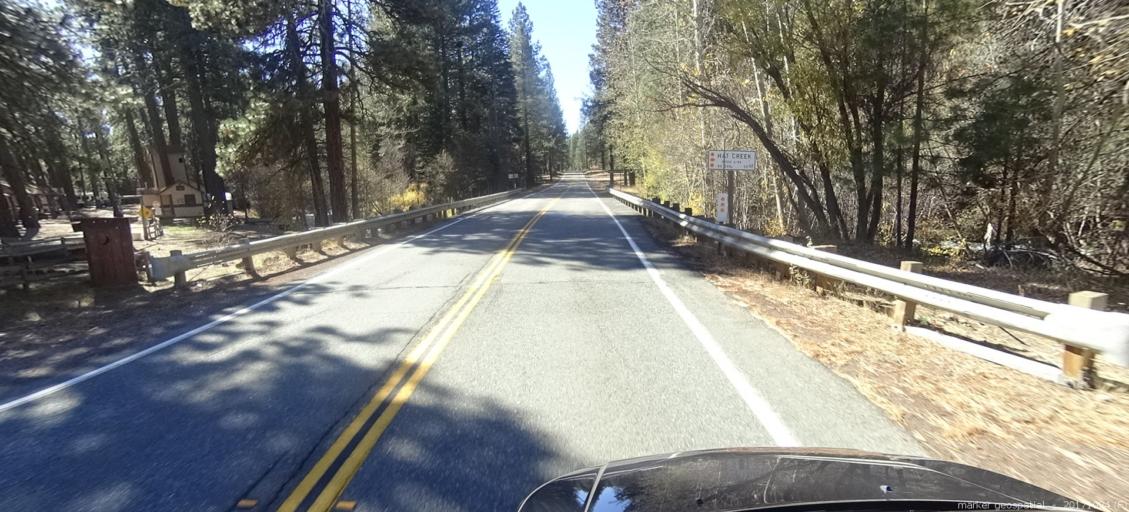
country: US
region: California
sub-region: Shasta County
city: Burney
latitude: 40.6512
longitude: -121.4603
